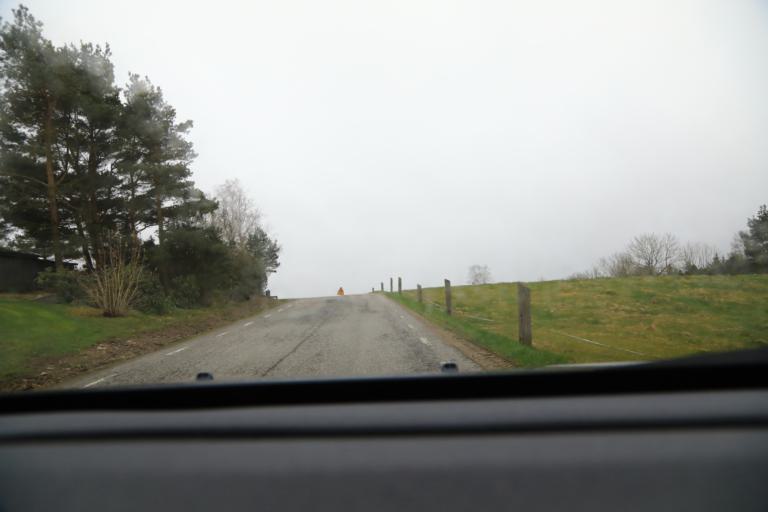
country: SE
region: Halland
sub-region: Kungsbacka Kommun
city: Frillesas
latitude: 57.2719
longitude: 12.2003
